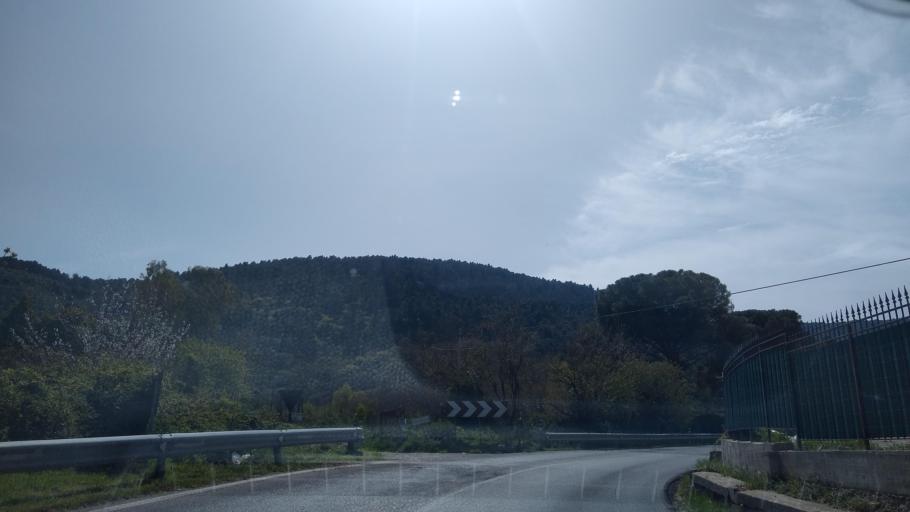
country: IT
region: Sicily
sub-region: Palermo
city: Pioppo
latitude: 38.0370
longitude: 13.2132
